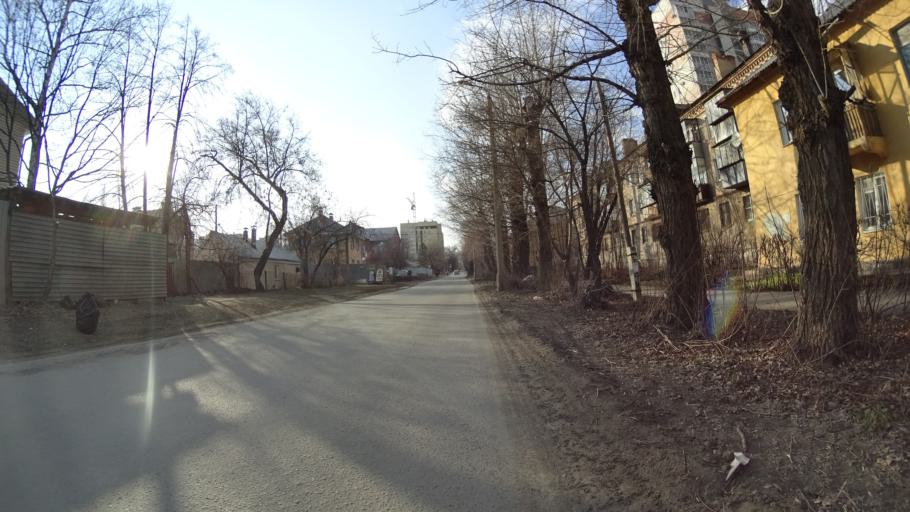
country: RU
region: Chelyabinsk
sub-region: Gorod Chelyabinsk
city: Chelyabinsk
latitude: 55.1400
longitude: 61.3891
